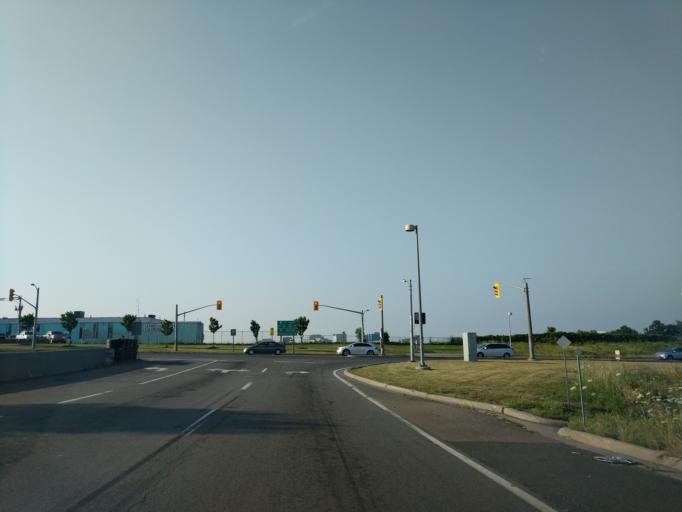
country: CA
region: Ontario
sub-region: York
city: Richmond Hill
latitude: 43.8664
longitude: -79.3729
